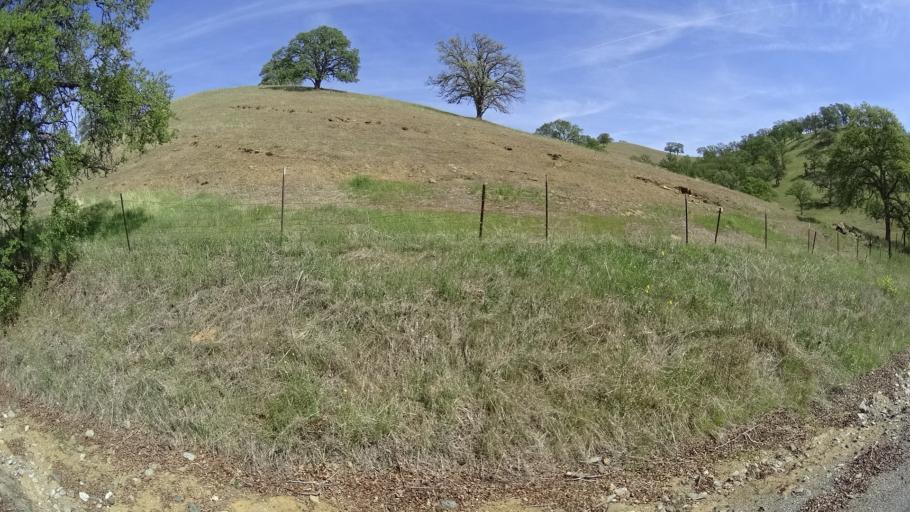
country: US
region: California
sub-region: Glenn County
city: Willows
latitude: 39.5647
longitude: -122.4407
